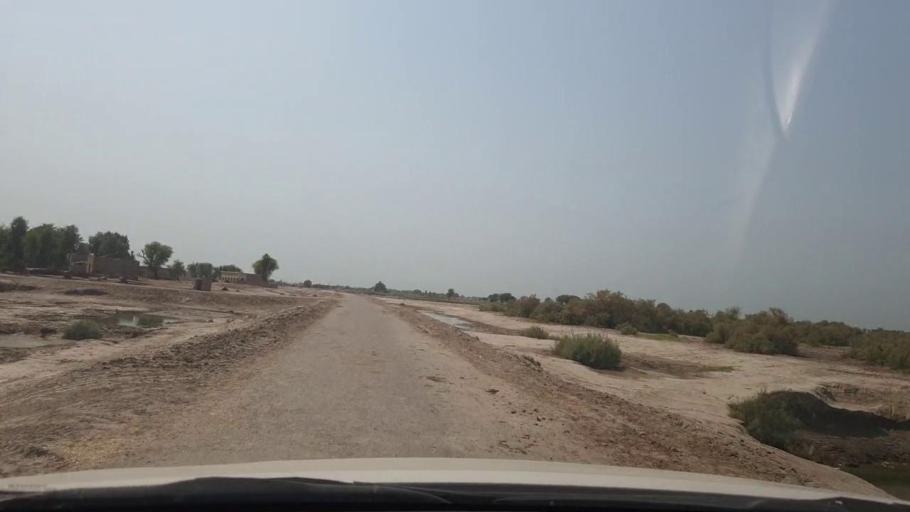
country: PK
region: Sindh
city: Shikarpur
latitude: 28.0080
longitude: 68.7098
